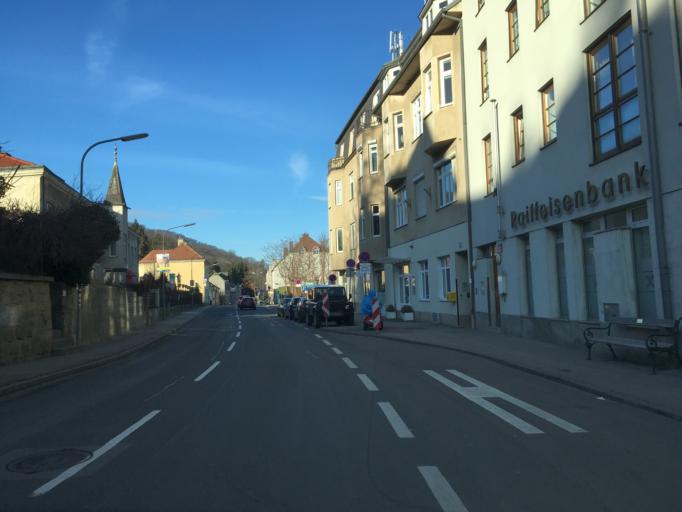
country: AT
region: Lower Austria
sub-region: Politischer Bezirk Korneuburg
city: Korneuburg
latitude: 48.3363
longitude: 16.2979
